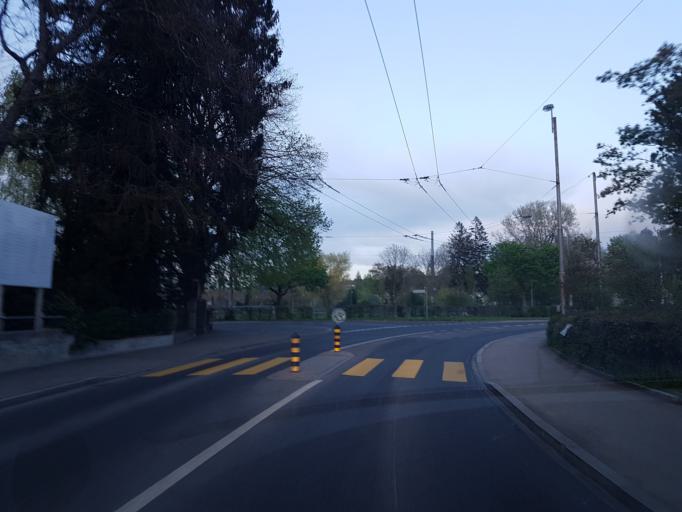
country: CH
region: Bern
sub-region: Biel/Bienne District
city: Biel/Bienne
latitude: 47.1476
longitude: 7.2688
